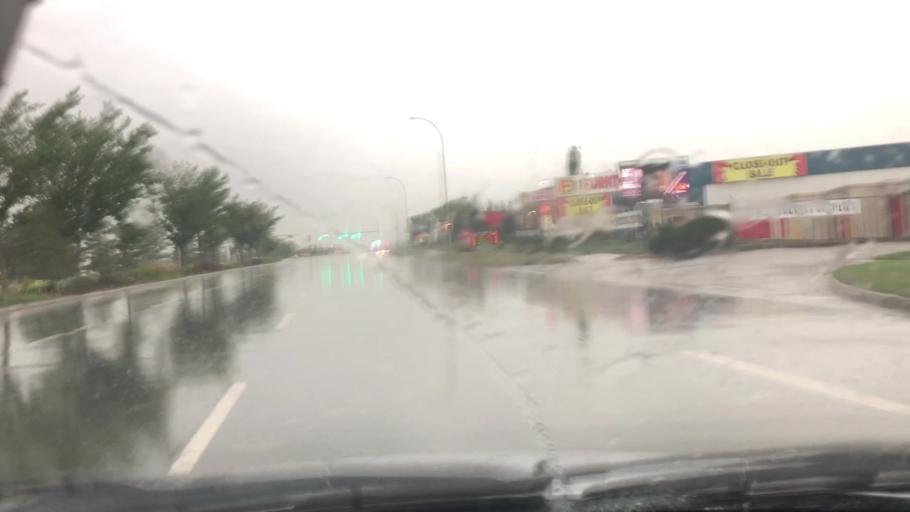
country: CA
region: Alberta
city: St. Albert
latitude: 53.5958
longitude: -113.5711
